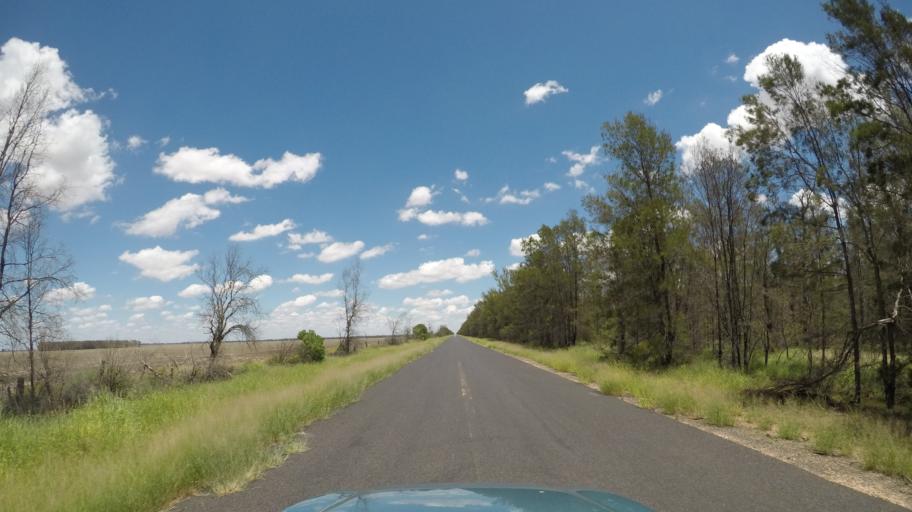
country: AU
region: Queensland
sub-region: Goondiwindi
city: Goondiwindi
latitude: -28.1656
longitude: 150.4384
